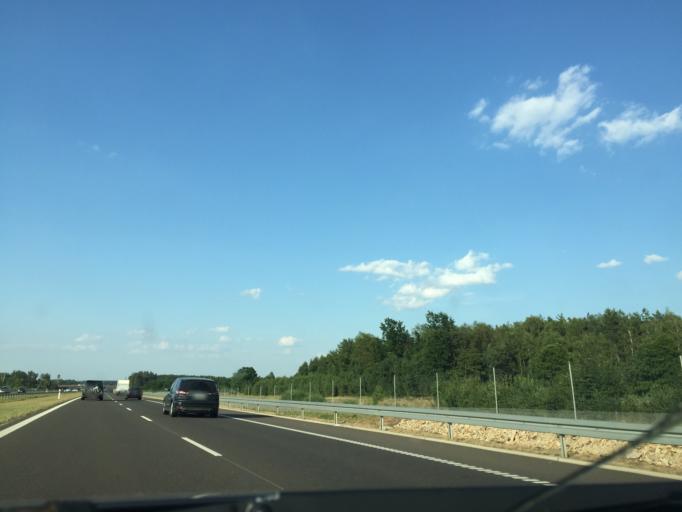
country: PL
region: Masovian Voivodeship
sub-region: Powiat radomski
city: Jedlinsk
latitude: 51.4820
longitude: 21.0636
